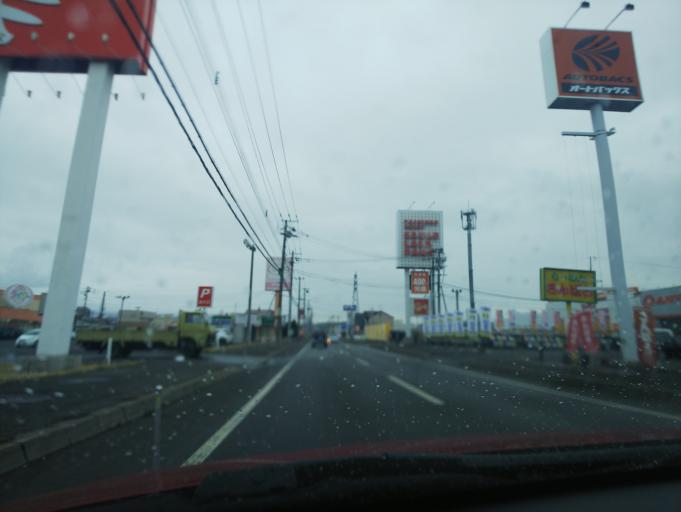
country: JP
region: Hokkaido
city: Nayoro
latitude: 44.3363
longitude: 142.4534
